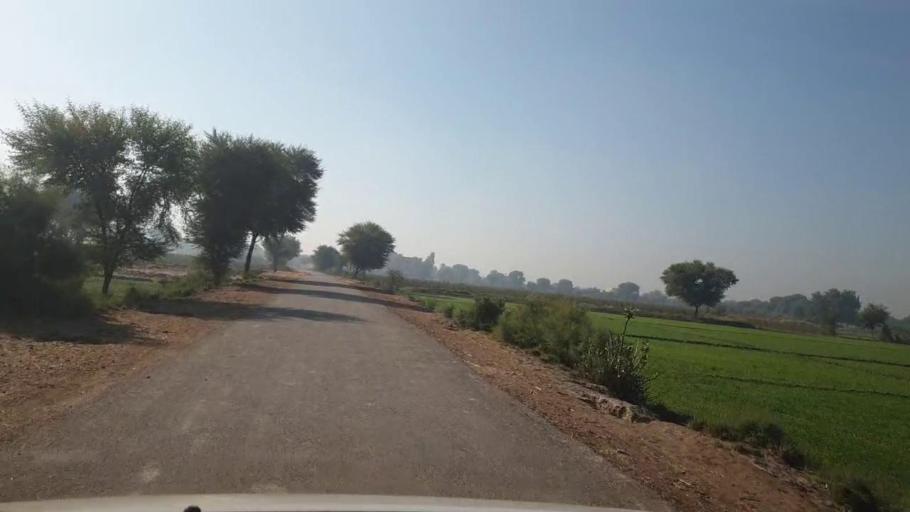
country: PK
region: Sindh
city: Dadu
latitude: 26.6533
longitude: 67.8224
